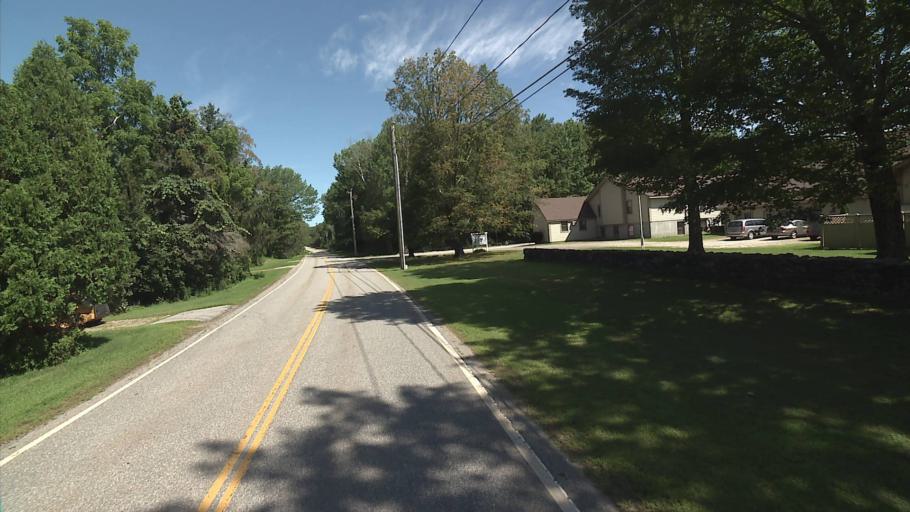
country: US
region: Connecticut
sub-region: Windham County
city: Windham
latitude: 41.7078
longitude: -72.0673
